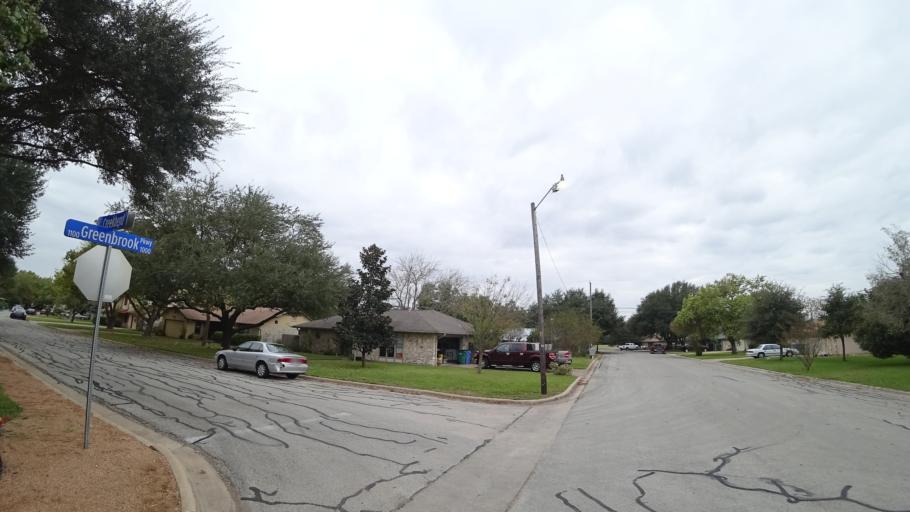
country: US
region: Texas
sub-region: Travis County
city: Pflugerville
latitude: 30.4511
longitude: -97.6226
